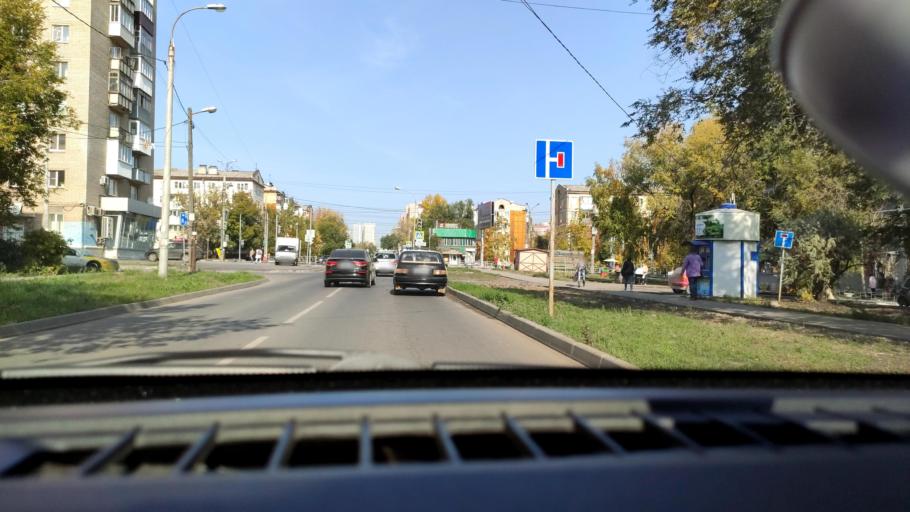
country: RU
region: Samara
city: Samara
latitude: 53.2001
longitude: 50.2037
